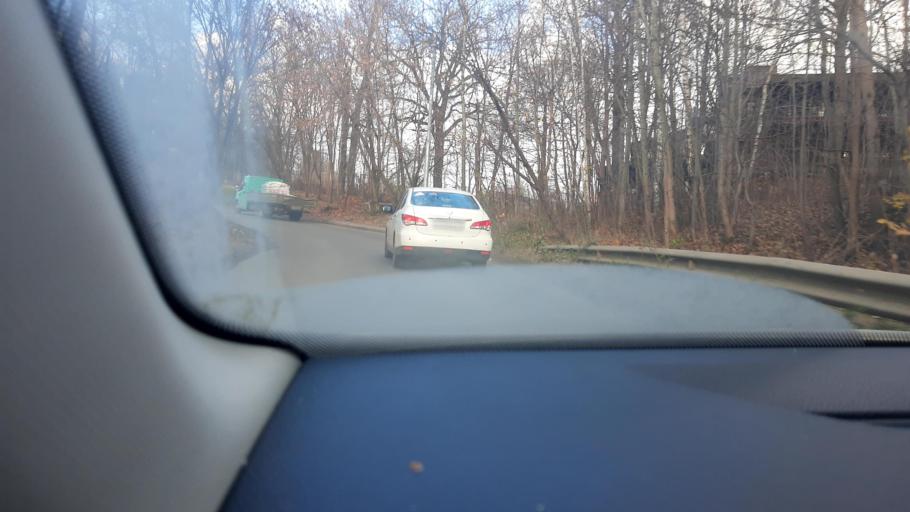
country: RU
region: Moskovskaya
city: Biryulevo Zapadnoye
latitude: 55.5597
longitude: 37.6406
